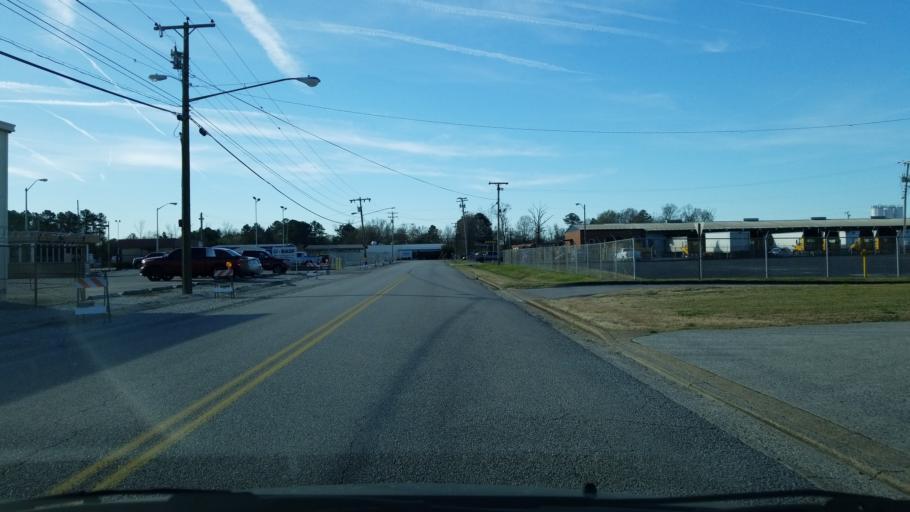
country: US
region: Tennessee
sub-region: Hamilton County
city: East Chattanooga
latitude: 35.0461
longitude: -85.1932
